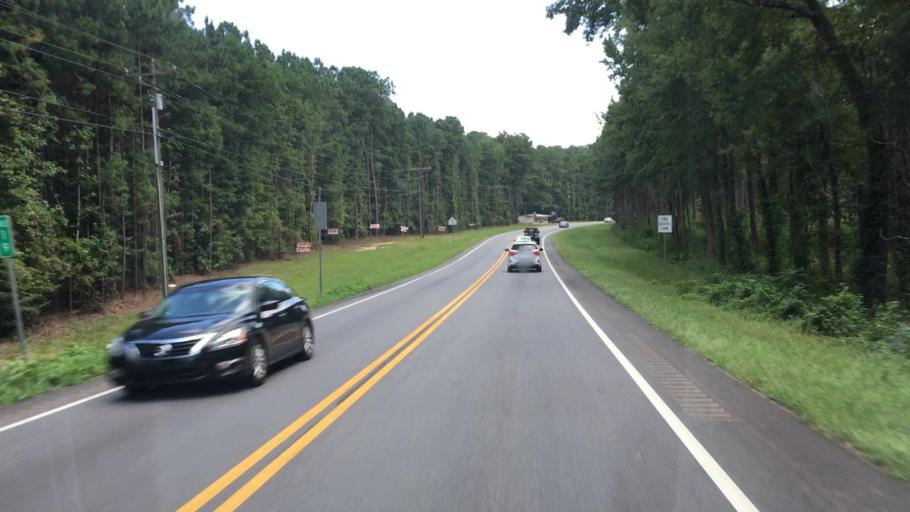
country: US
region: Georgia
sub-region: Putnam County
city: Jefferson
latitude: 33.4081
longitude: -83.3689
